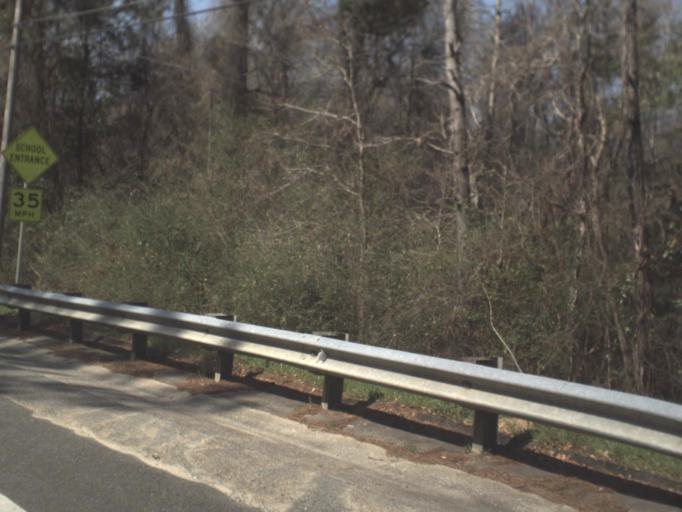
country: US
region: Florida
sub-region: Gadsden County
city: Quincy
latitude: 30.5951
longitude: -84.5459
